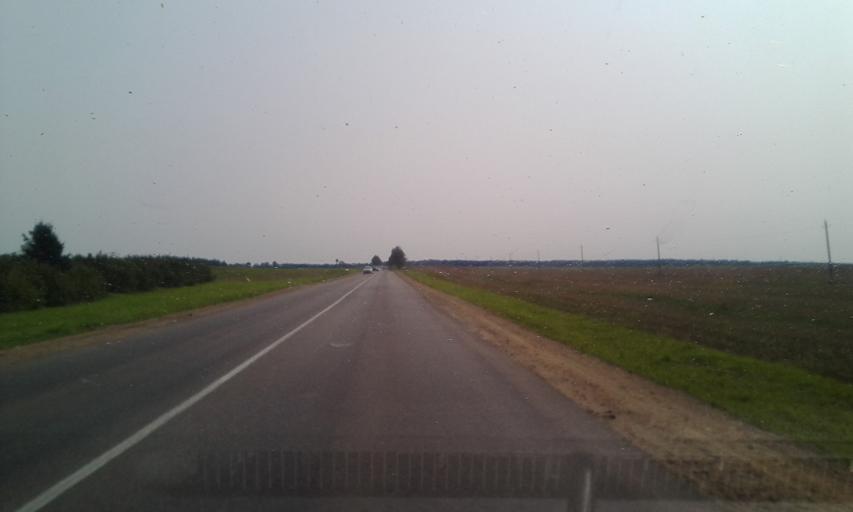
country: BY
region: Minsk
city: Hatava
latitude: 53.8288
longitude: 27.6177
